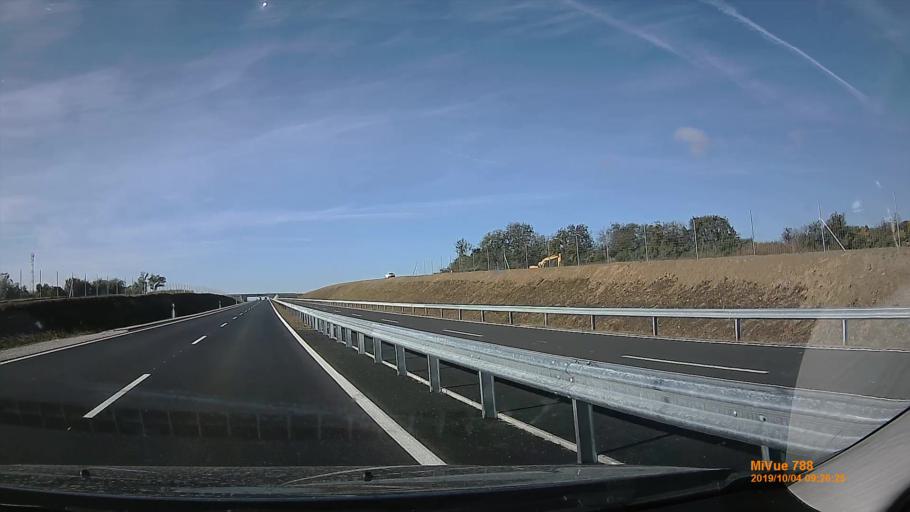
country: HU
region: Somogy
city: Kaposvar
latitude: 46.5170
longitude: 17.8147
